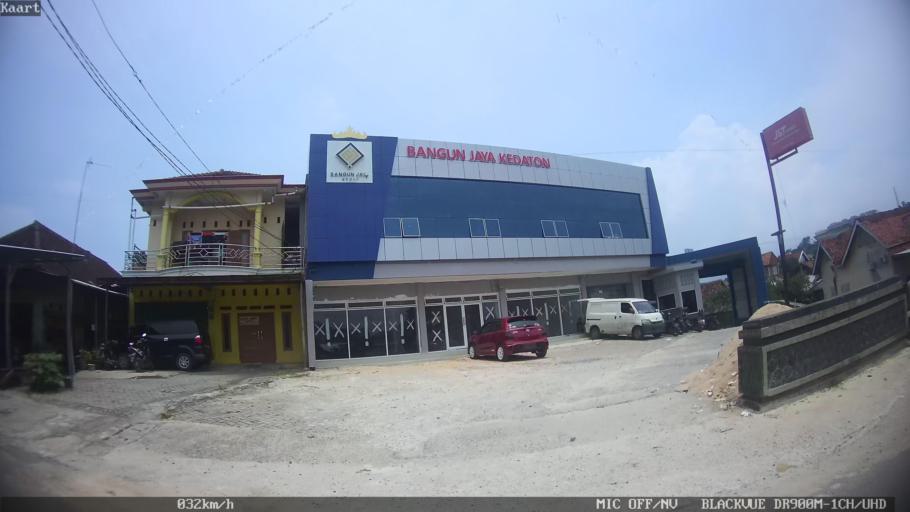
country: ID
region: Lampung
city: Bandarlampung
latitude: -5.4119
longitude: 105.2708
